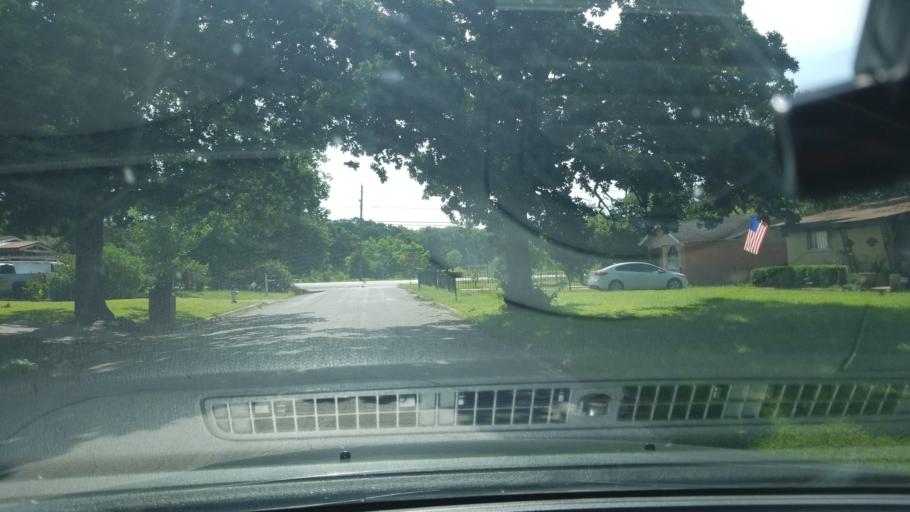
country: US
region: Texas
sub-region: Dallas County
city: Balch Springs
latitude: 32.7330
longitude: -96.6400
